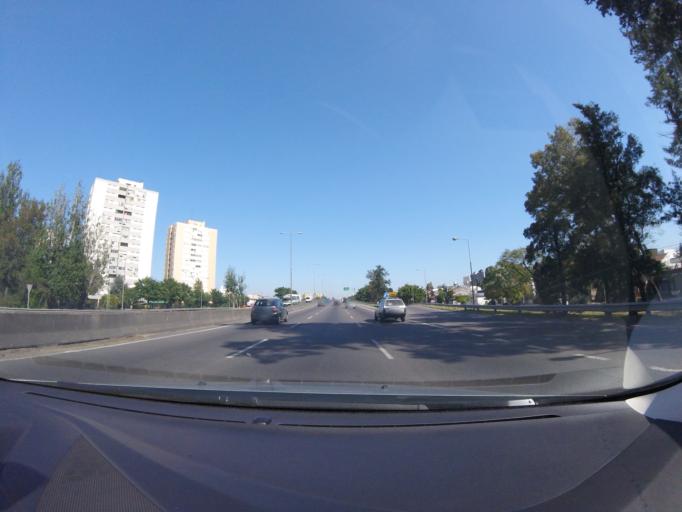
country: AR
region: Buenos Aires F.D.
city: Villa Lugano
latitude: -34.6925
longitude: -58.4775
